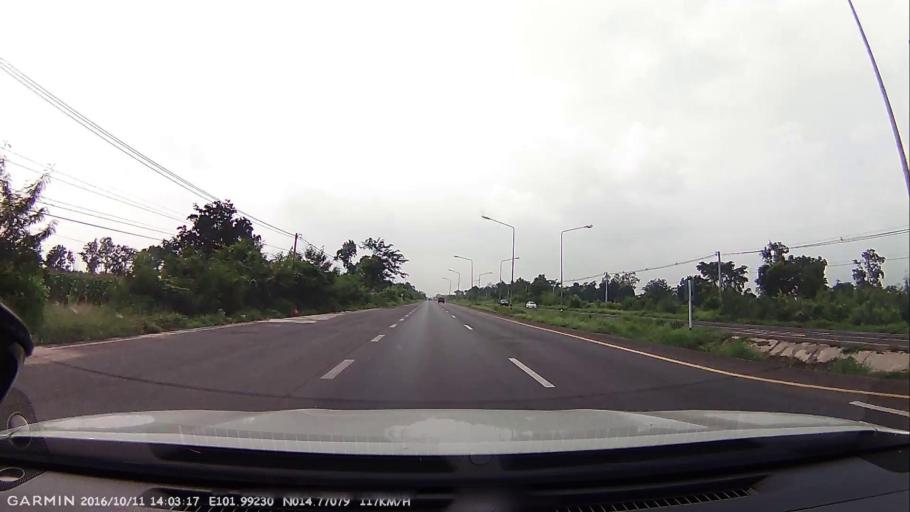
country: TH
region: Nakhon Ratchasima
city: Pak Thong Chai
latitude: 14.7708
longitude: 101.9924
